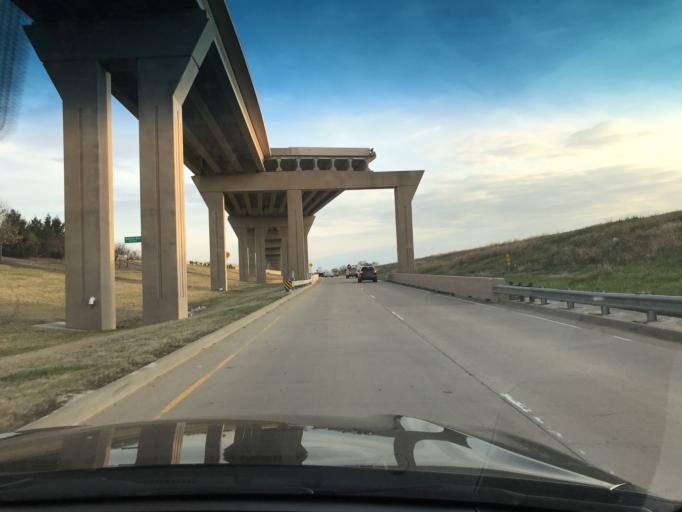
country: US
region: Texas
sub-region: Tarrant County
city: Benbrook
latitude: 32.6809
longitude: -97.4070
